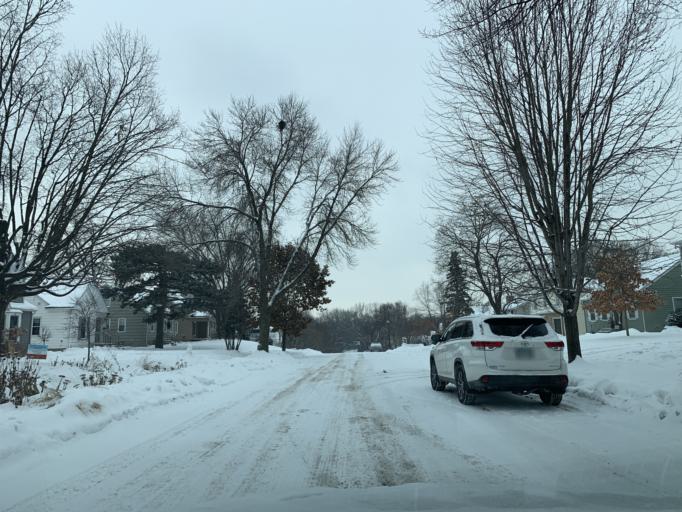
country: US
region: Minnesota
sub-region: Hennepin County
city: Saint Louis Park
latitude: 44.9305
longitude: -93.3367
